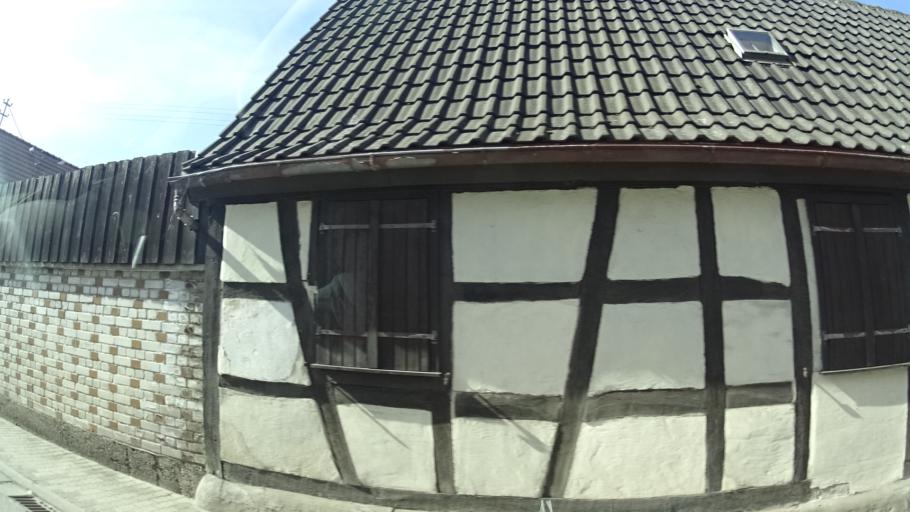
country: DE
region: Rheinland-Pfalz
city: Gommersheim
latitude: 49.3024
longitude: 8.2622
